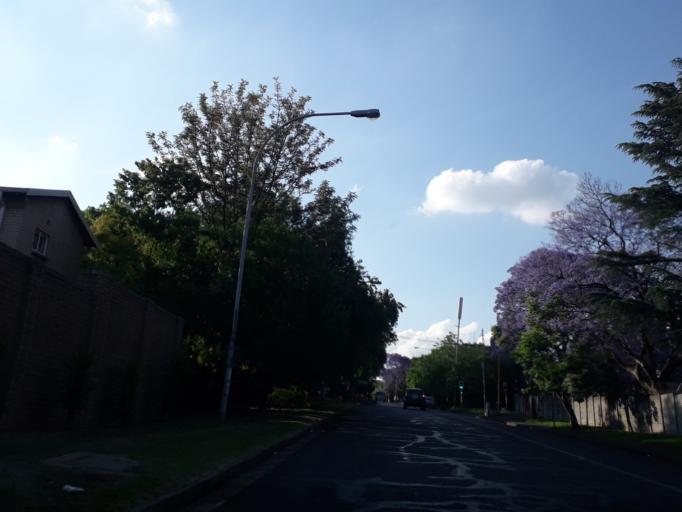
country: ZA
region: Gauteng
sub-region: City of Johannesburg Metropolitan Municipality
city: Johannesburg
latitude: -26.1428
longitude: 28.0015
